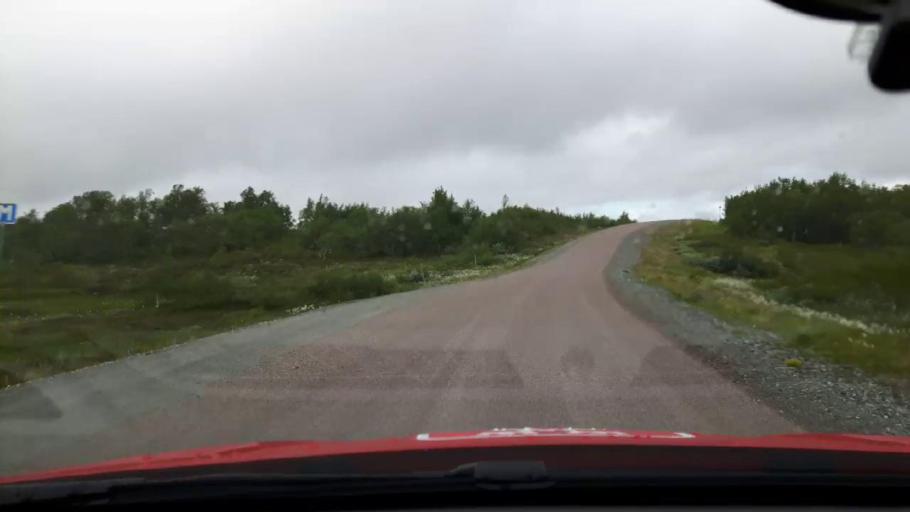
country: NO
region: Nord-Trondelag
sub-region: Meraker
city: Meraker
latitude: 63.2142
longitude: 12.4047
